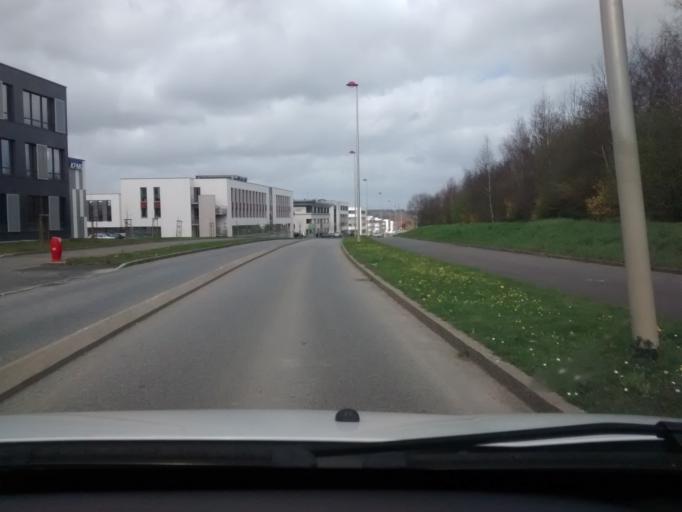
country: FR
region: Brittany
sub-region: Departement d'Ille-et-Vilaine
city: Saint-Gregoire
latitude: 48.1494
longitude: -1.6973
